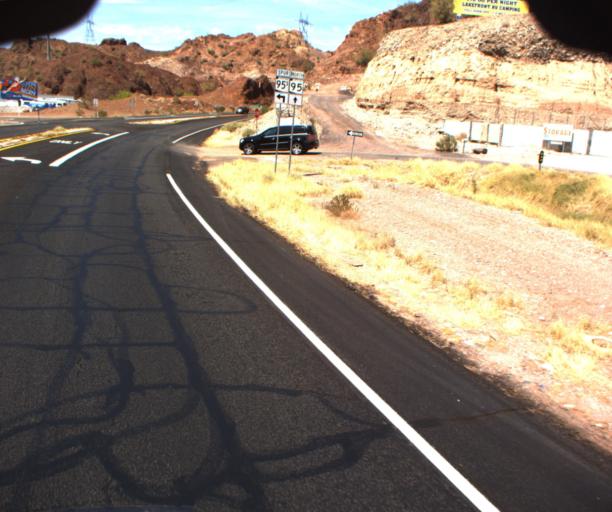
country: US
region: Arizona
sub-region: La Paz County
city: Cienega Springs
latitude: 34.2849
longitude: -114.1346
